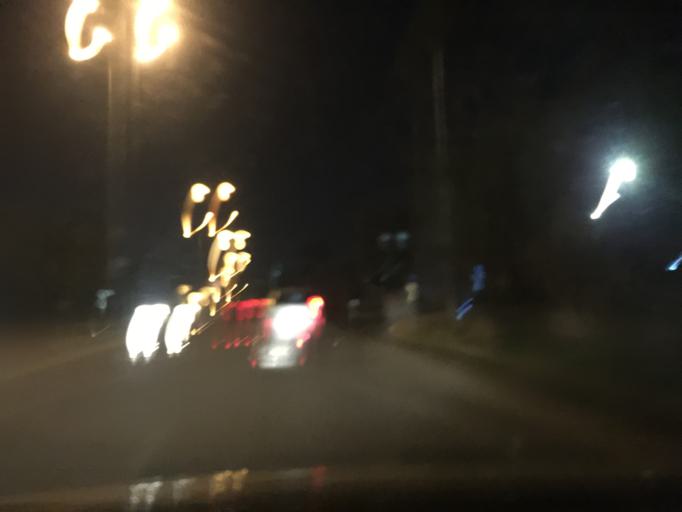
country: JO
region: Amman
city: Al Jubayhah
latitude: 32.0301
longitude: 35.8876
